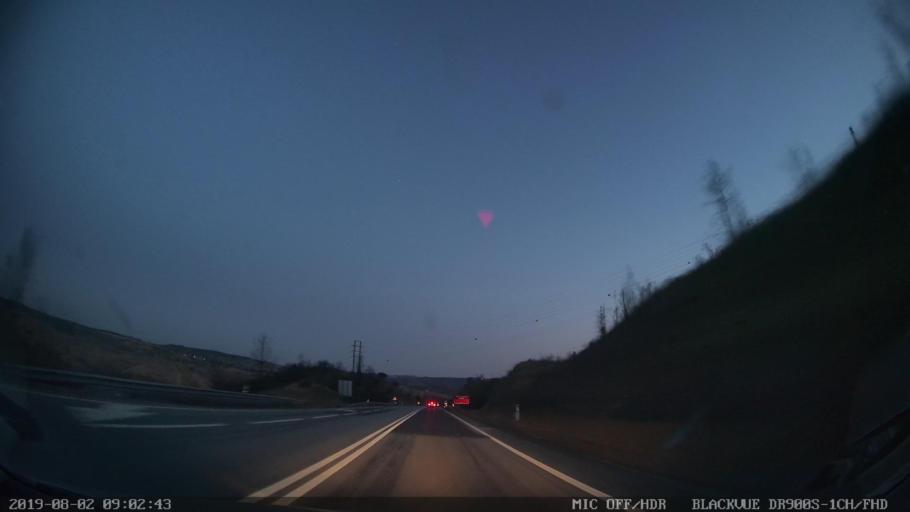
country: PT
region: Portalegre
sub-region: Nisa
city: Nisa
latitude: 39.5531
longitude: -7.7938
